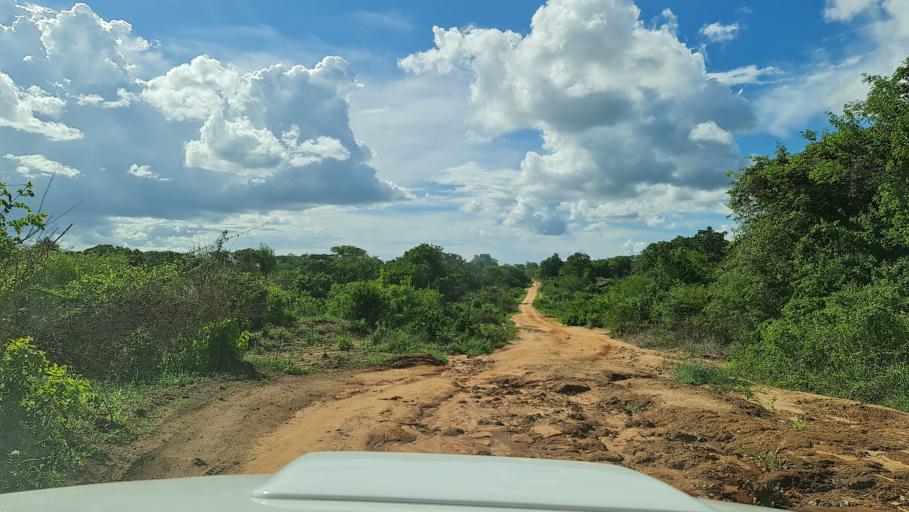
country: MZ
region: Nampula
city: Ilha de Mocambique
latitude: -15.4168
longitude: 40.2601
